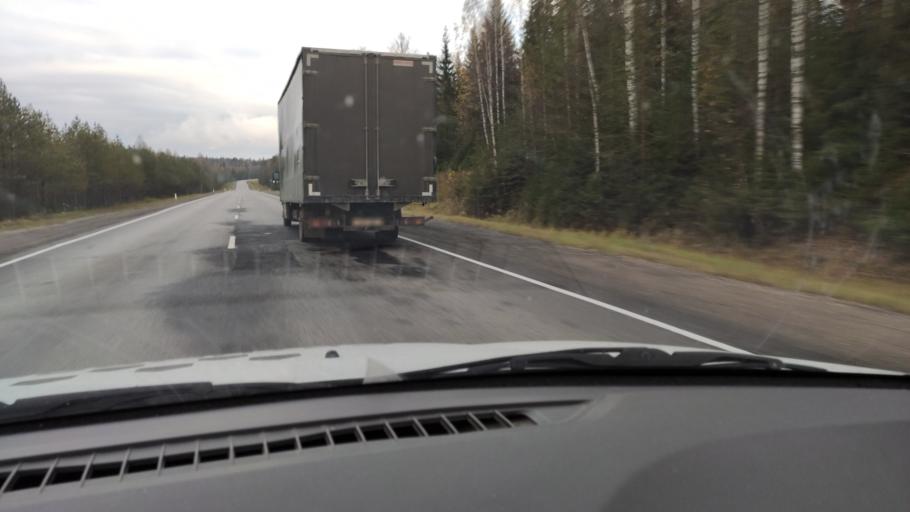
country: RU
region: Kirov
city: Chernaya Kholunitsa
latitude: 58.8242
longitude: 51.7929
